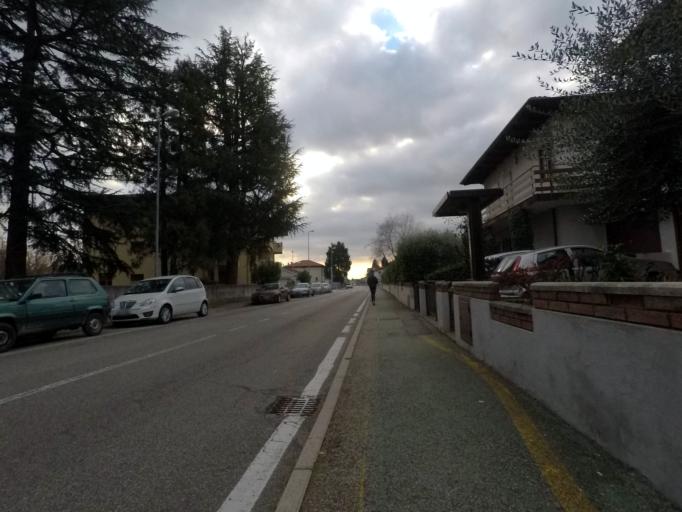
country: IT
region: Friuli Venezia Giulia
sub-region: Provincia di Udine
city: Feletto Umberto
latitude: 46.1064
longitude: 13.2149
